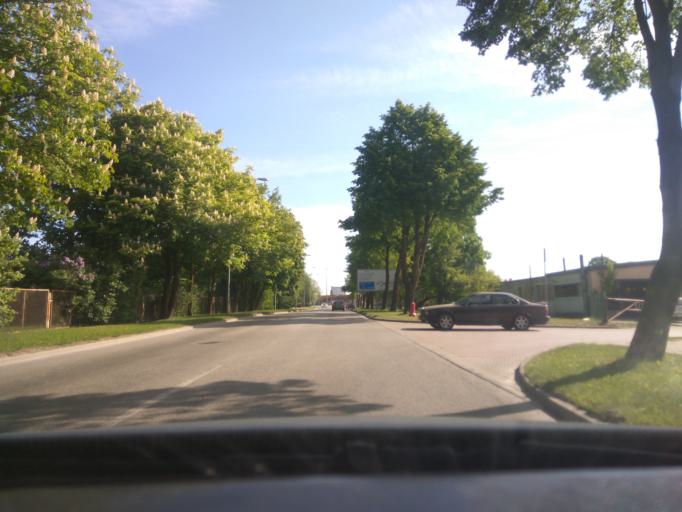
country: LV
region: Ventspils
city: Ventspils
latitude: 57.3833
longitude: 21.5839
